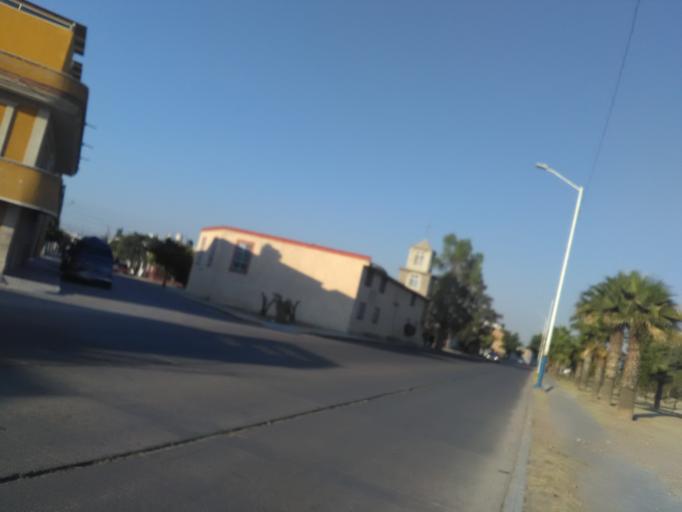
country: MX
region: Durango
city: Victoria de Durango
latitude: 24.0398
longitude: -104.6520
